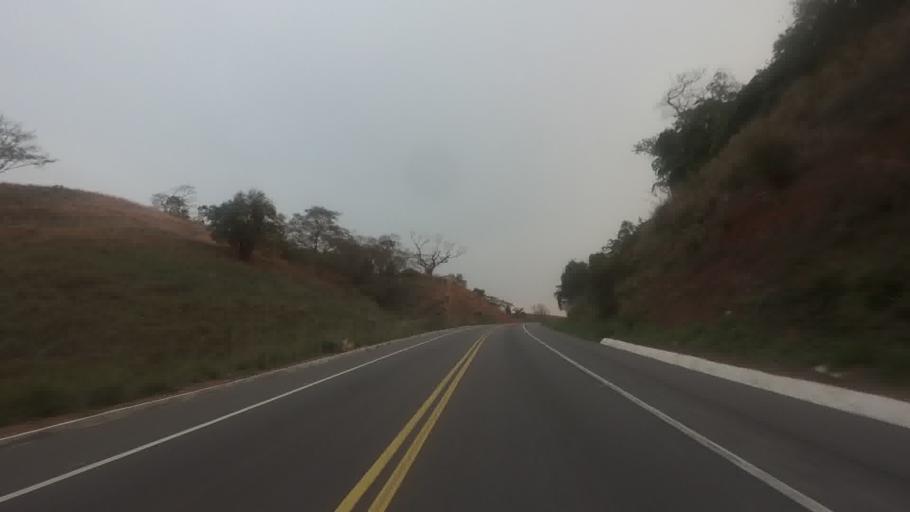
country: BR
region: Minas Gerais
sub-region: Recreio
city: Recreio
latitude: -21.7141
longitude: -42.4275
